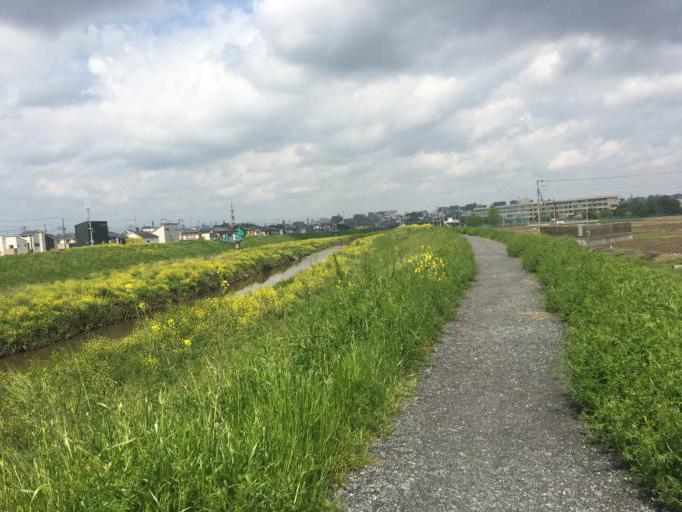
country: JP
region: Saitama
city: Kawagoe
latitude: 35.8974
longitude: 139.5032
